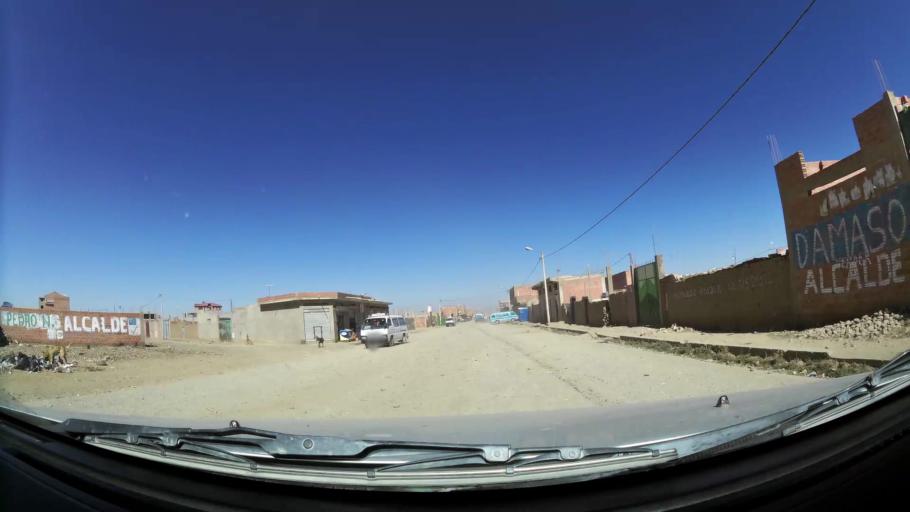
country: BO
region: La Paz
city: La Paz
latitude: -16.6205
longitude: -68.1850
